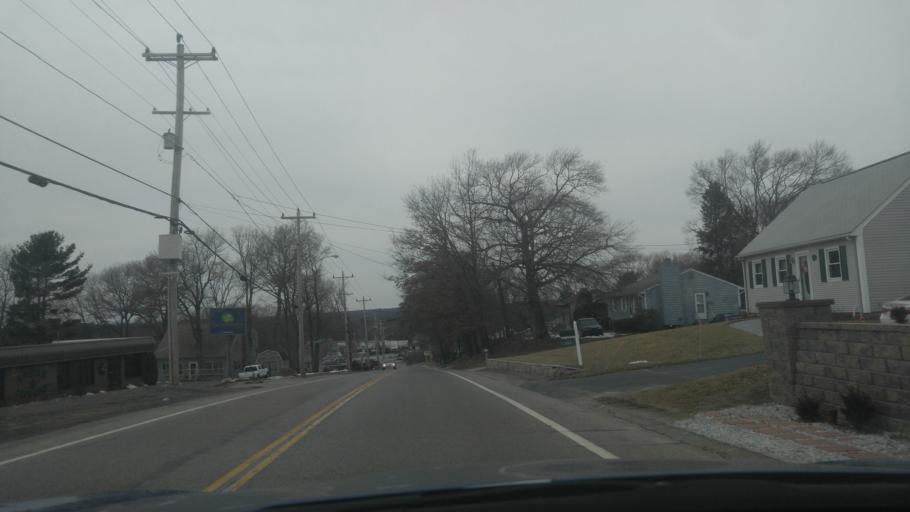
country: US
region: Rhode Island
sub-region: Kent County
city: West Warwick
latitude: 41.6833
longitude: -71.5445
